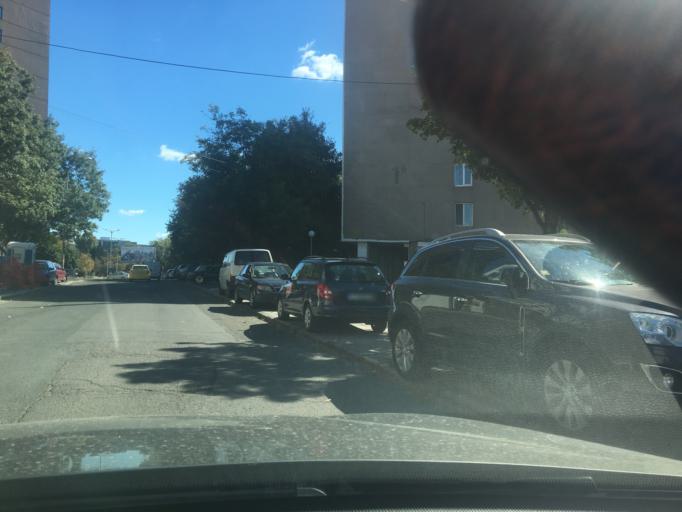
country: BG
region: Burgas
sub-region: Obshtina Burgas
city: Burgas
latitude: 42.5177
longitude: 27.4585
